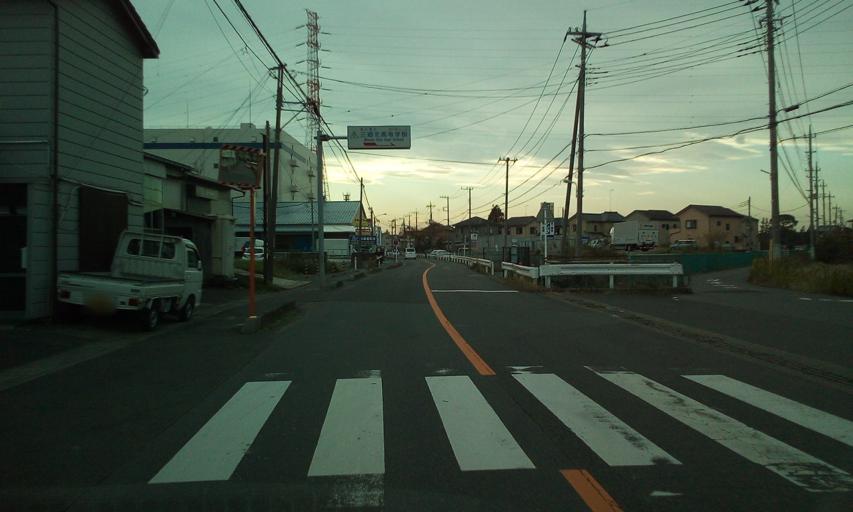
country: JP
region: Chiba
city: Nagareyama
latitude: 35.8423
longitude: 139.8765
